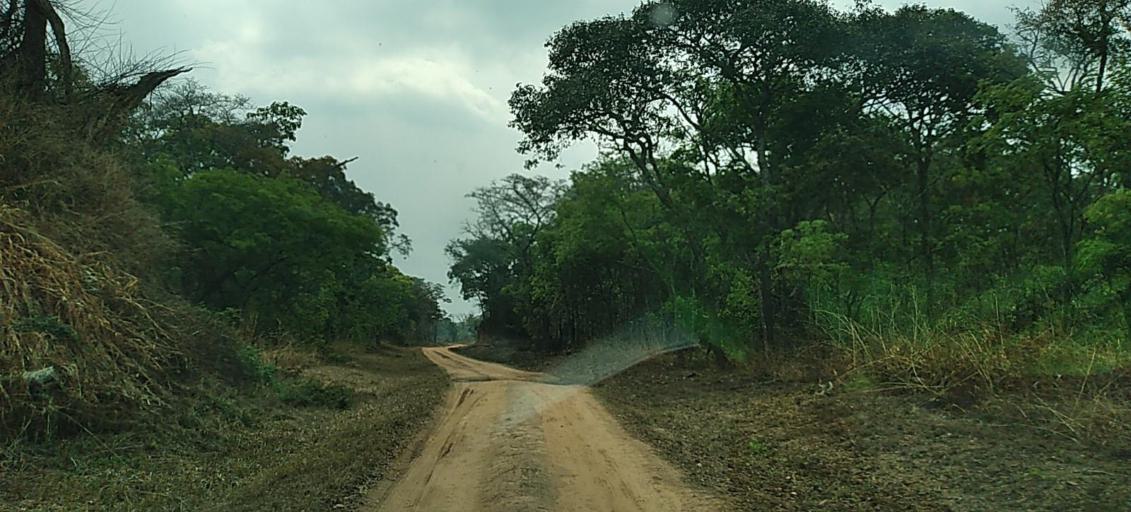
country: ZM
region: North-Western
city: Mwinilunga
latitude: -11.4685
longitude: 24.4809
